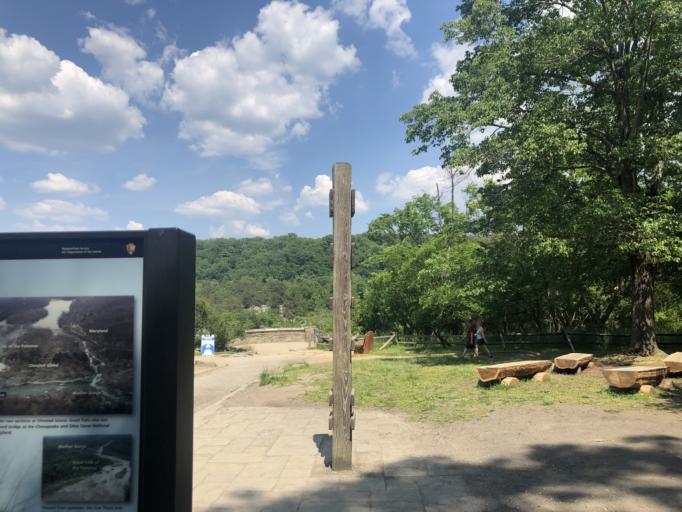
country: US
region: Virginia
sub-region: Fairfax County
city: Great Falls
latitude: 38.9950
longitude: -77.2532
